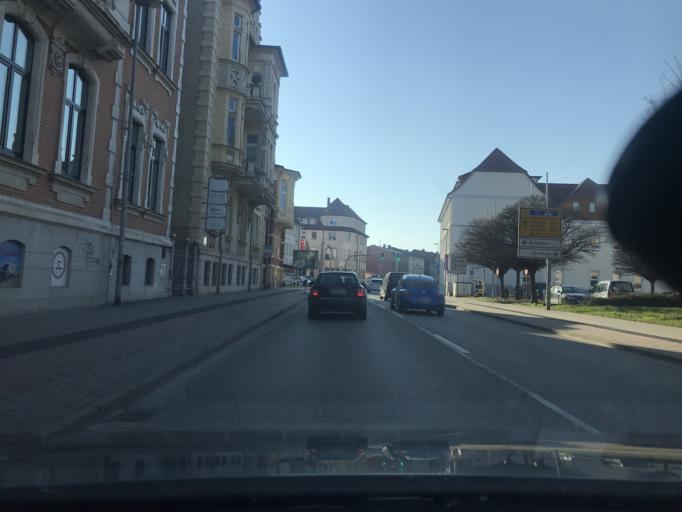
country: DE
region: Thuringia
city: Nordhausen
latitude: 51.4963
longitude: 10.7934
